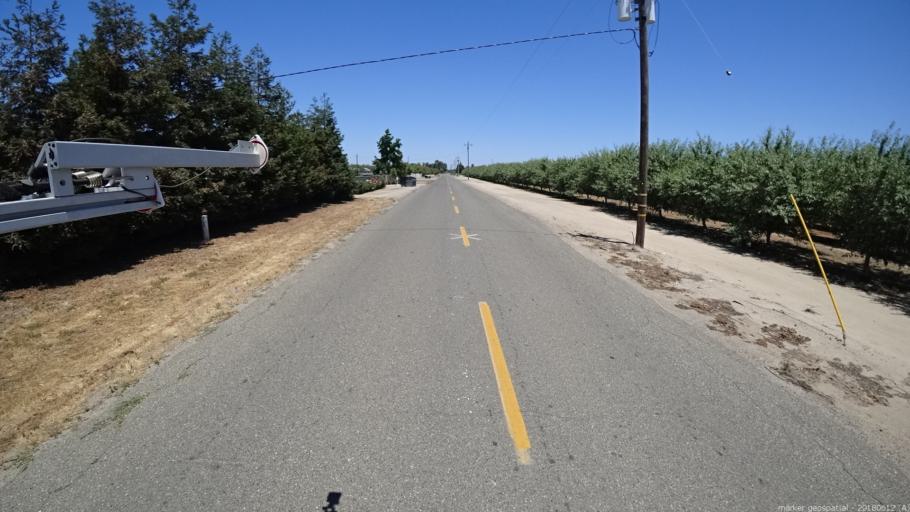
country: US
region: California
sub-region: Madera County
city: Chowchilla
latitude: 37.0961
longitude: -120.2746
